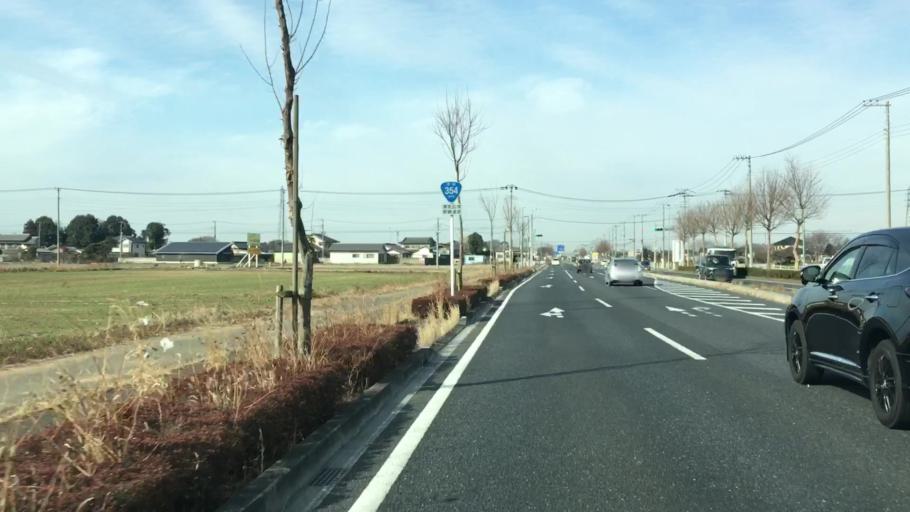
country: JP
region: Gunma
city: Tatebayashi
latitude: 36.2318
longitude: 139.4864
